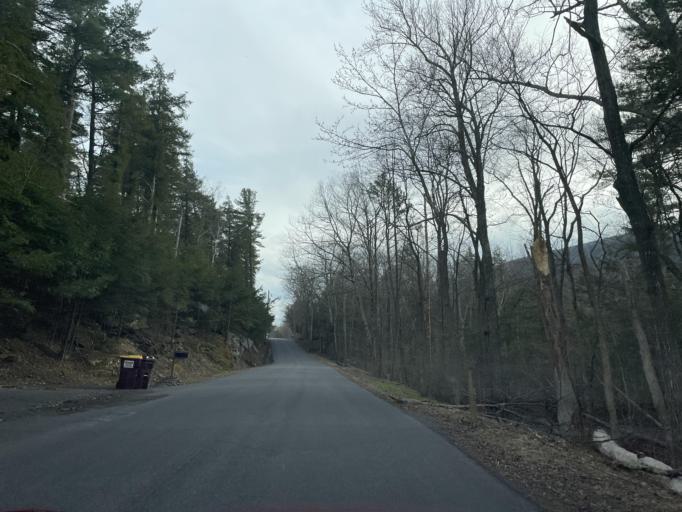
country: US
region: New York
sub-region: Ulster County
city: Manorville
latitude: 42.1583
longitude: -74.0287
